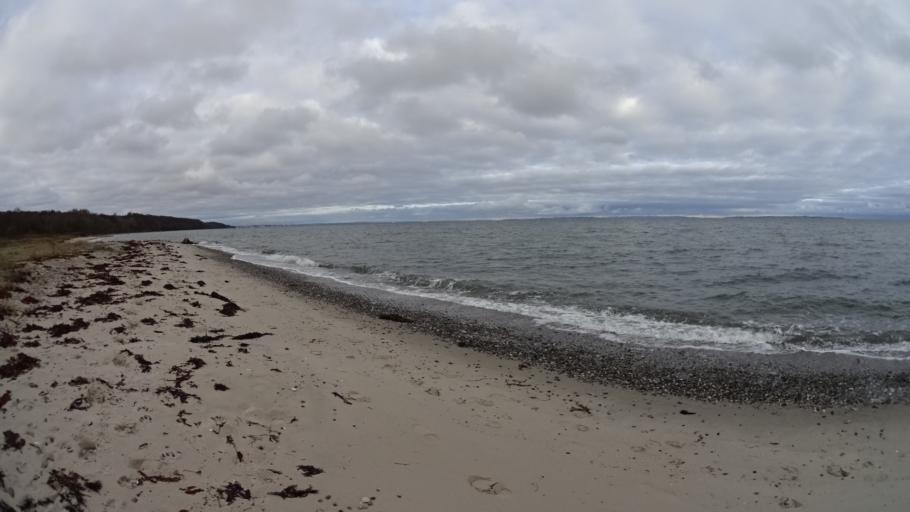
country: DK
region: Central Jutland
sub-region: Arhus Kommune
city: Beder
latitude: 56.0537
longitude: 10.2662
